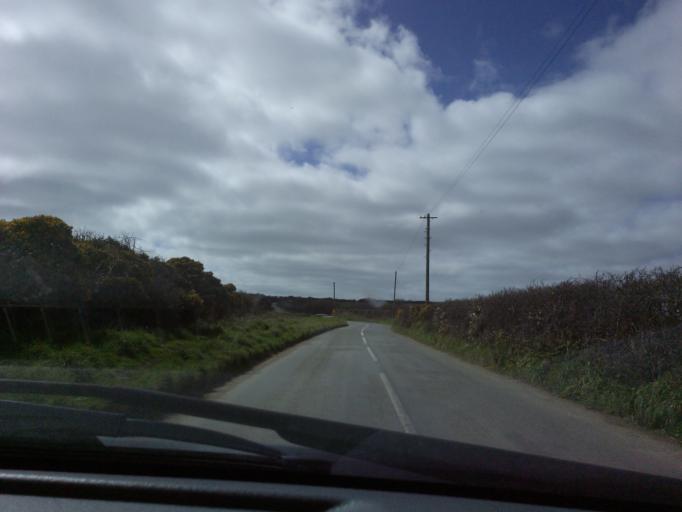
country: GB
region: England
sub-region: Cornwall
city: St. Buryan
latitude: 50.0647
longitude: -5.5910
